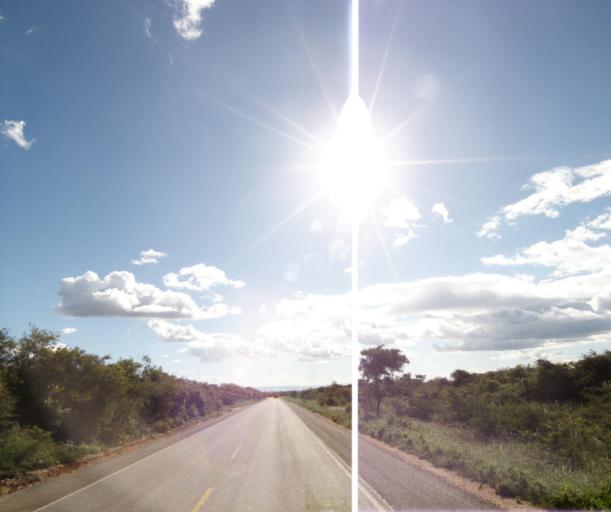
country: BR
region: Bahia
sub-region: Caetite
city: Caetite
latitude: -14.1313
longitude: -42.6305
